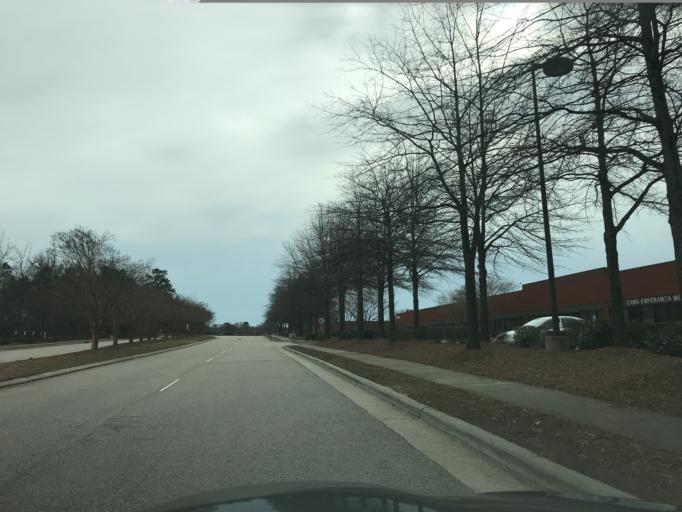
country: US
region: North Carolina
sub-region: Wake County
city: Raleigh
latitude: 35.8731
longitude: -78.5899
